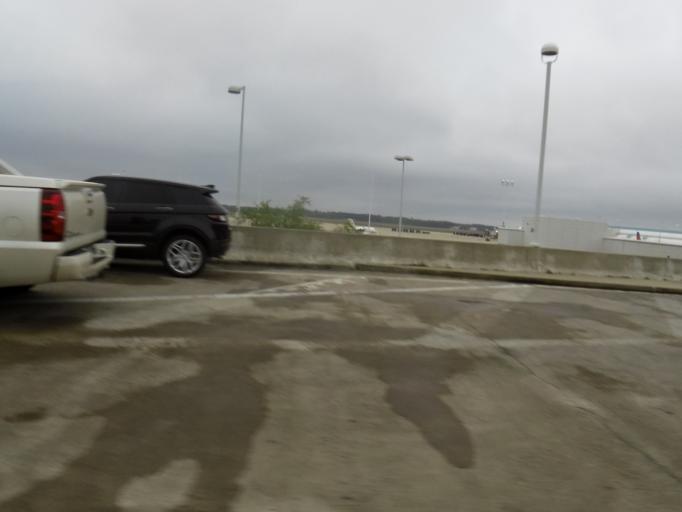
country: US
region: Florida
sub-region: Nassau County
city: Nassau Village-Ratliff
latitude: 30.4902
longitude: -81.6828
